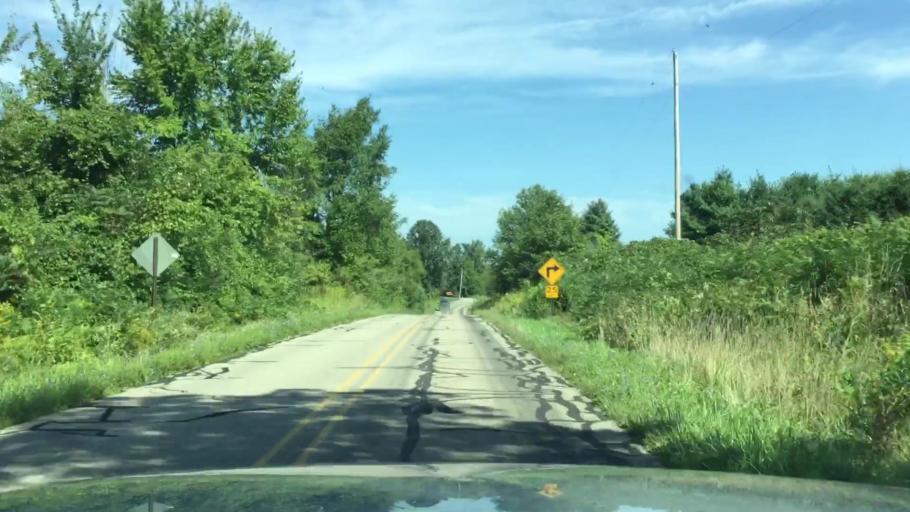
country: US
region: Michigan
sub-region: Lenawee County
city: Manitou Beach-Devils Lake
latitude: 41.9948
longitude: -84.3251
